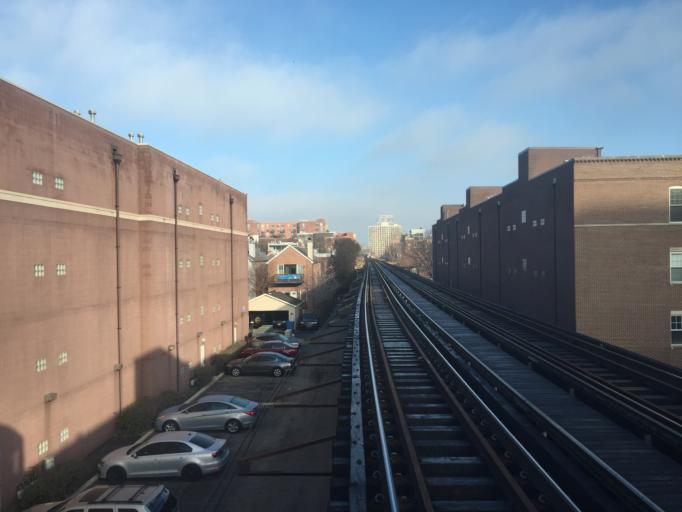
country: US
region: Illinois
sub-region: Cook County
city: Chicago
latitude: 41.9047
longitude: -87.6371
